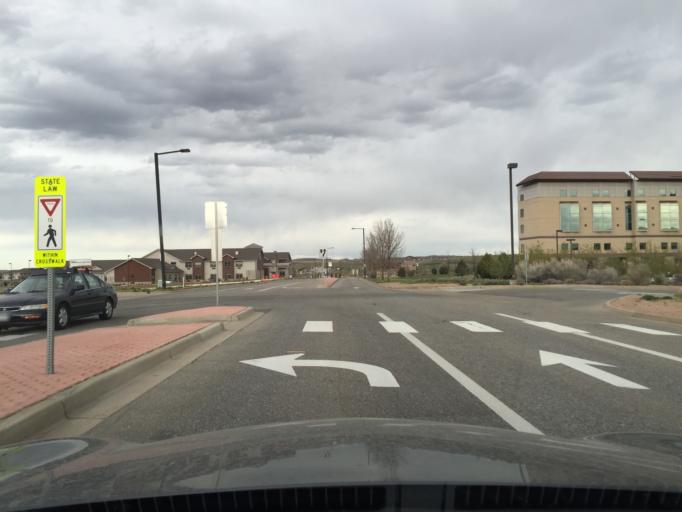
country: US
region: Colorado
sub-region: Boulder County
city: Lafayette
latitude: 39.9724
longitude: -105.0883
